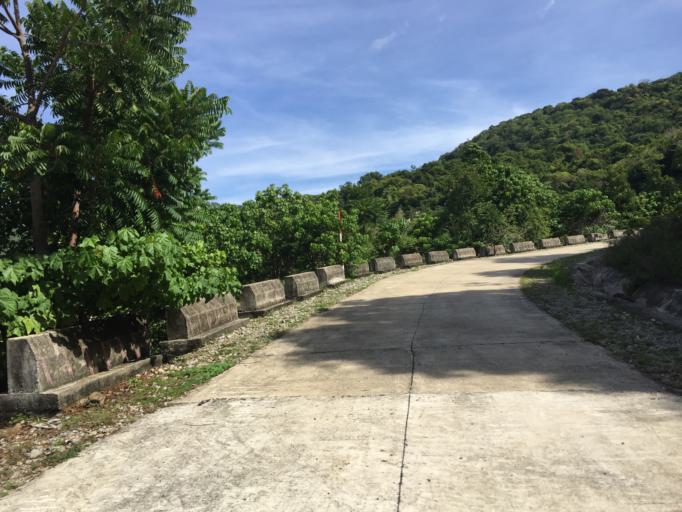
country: VN
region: Quang Nam
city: Hoi An
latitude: 15.9307
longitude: 108.5312
